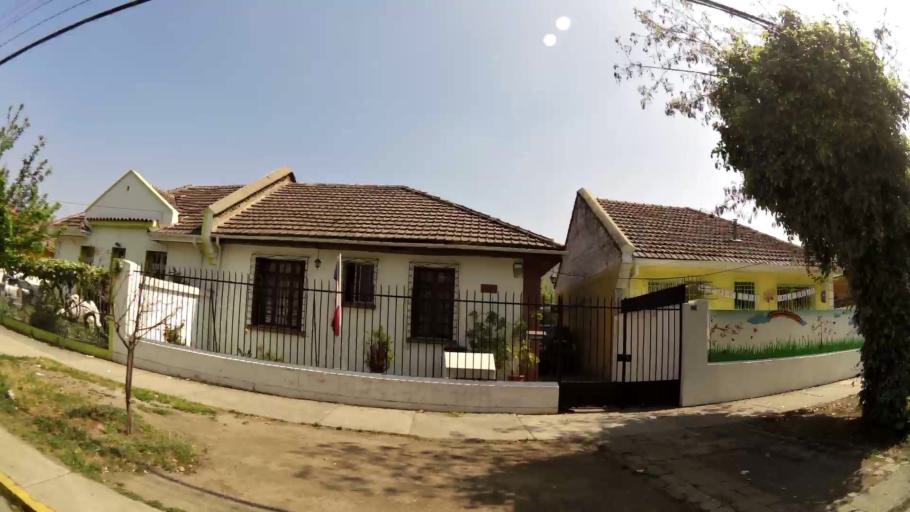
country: CL
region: Santiago Metropolitan
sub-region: Provincia de Santiago
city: Santiago
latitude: -33.4582
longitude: -70.6209
